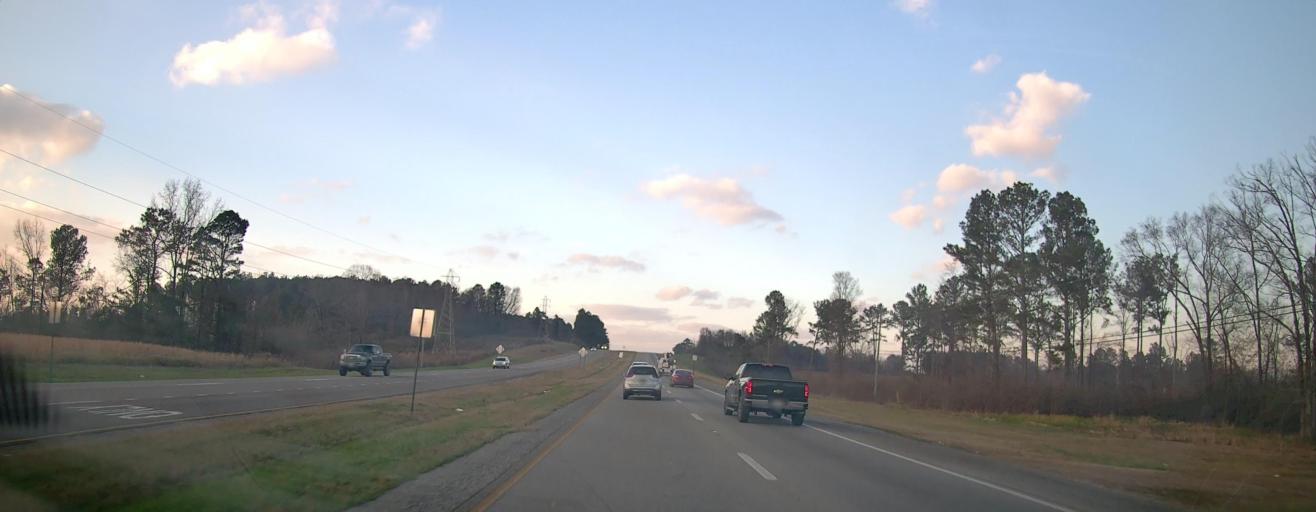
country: US
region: Alabama
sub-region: Calhoun County
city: Alexandria
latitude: 33.7890
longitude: -85.8980
